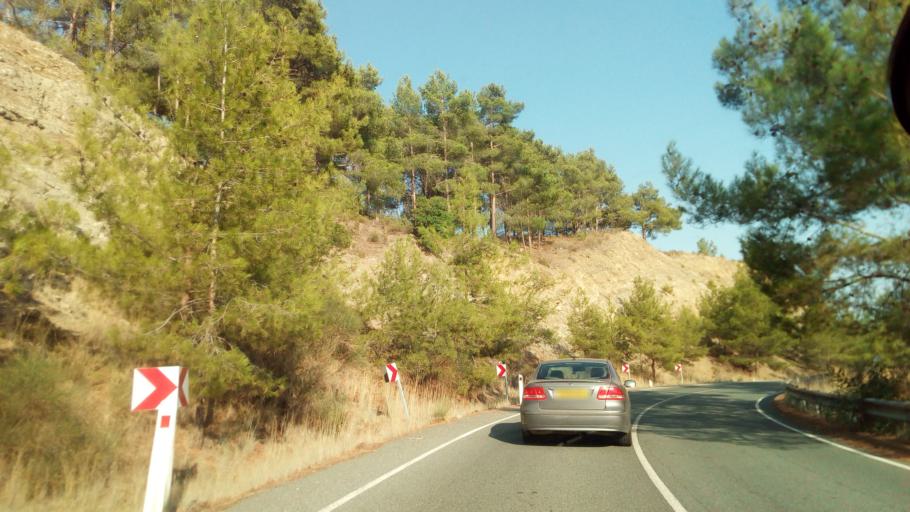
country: CY
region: Limassol
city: Pelendri
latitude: 34.8613
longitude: 32.8960
